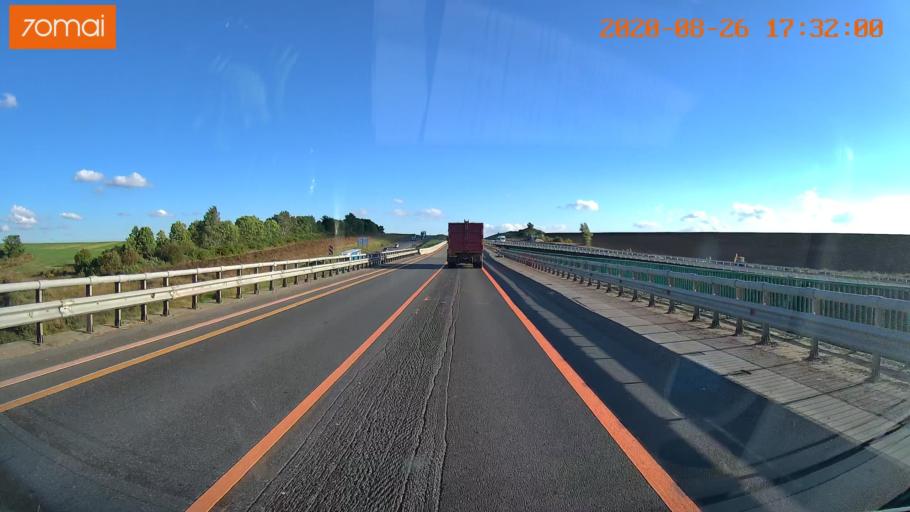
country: RU
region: Tula
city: Kazachka
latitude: 53.4274
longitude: 38.1811
